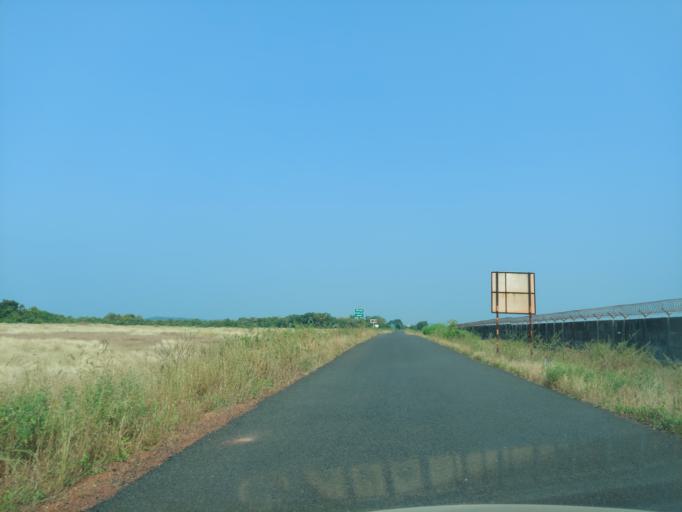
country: IN
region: Maharashtra
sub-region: Sindhudurg
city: Malvan
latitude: 15.9991
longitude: 73.5086
